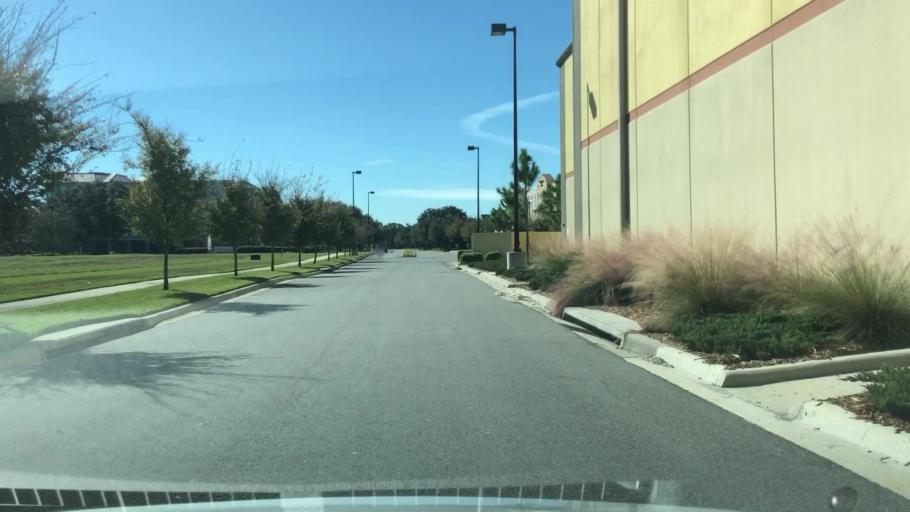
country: US
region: Florida
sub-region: Orange County
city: Conway
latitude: 28.4638
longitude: -81.3046
